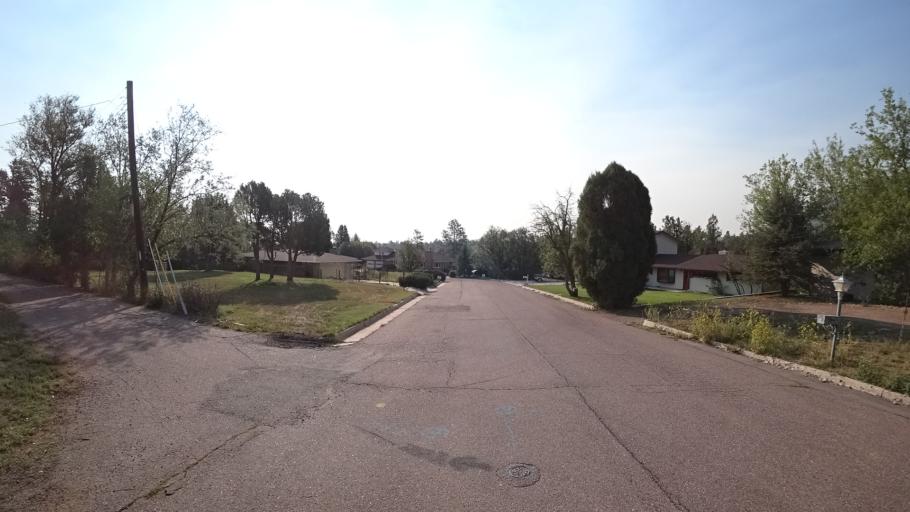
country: US
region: Colorado
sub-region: El Paso County
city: Colorado Springs
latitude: 38.7996
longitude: -104.8549
